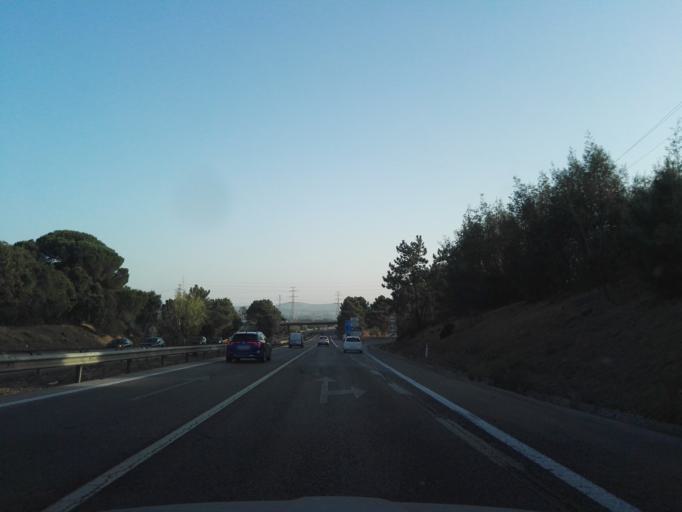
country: PT
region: Setubal
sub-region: Barreiro
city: Santo Antonio da Charneca
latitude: 38.5912
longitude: -9.0202
